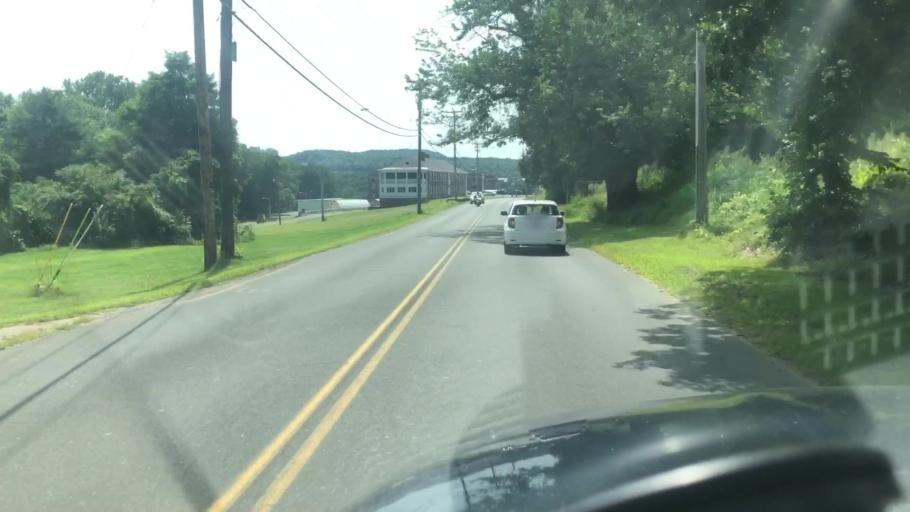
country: US
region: Massachusetts
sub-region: Hampden County
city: Westfield
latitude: 42.1139
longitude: -72.7005
